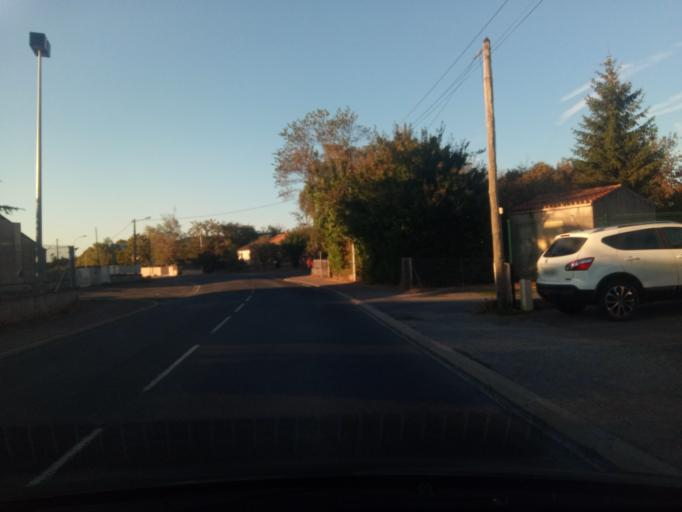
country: FR
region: Poitou-Charentes
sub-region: Departement de la Vienne
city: Montmorillon
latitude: 46.4218
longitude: 0.8610
